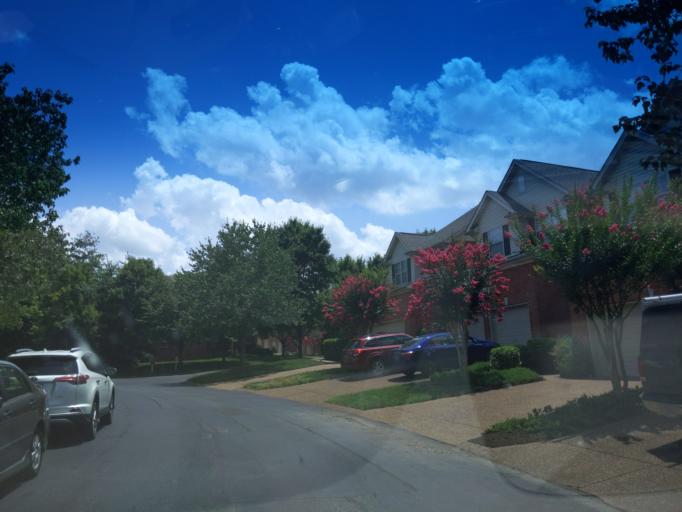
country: US
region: Tennessee
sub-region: Williamson County
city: Brentwood
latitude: 36.0389
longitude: -86.7656
